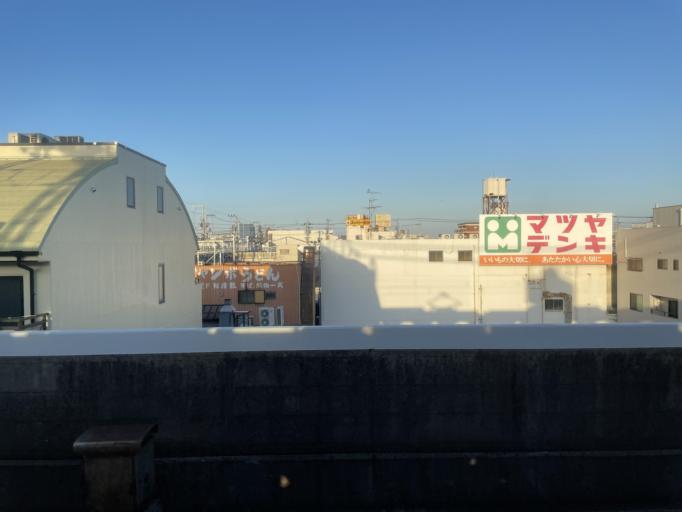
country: JP
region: Osaka
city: Matsubara
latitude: 34.6178
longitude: 135.5329
